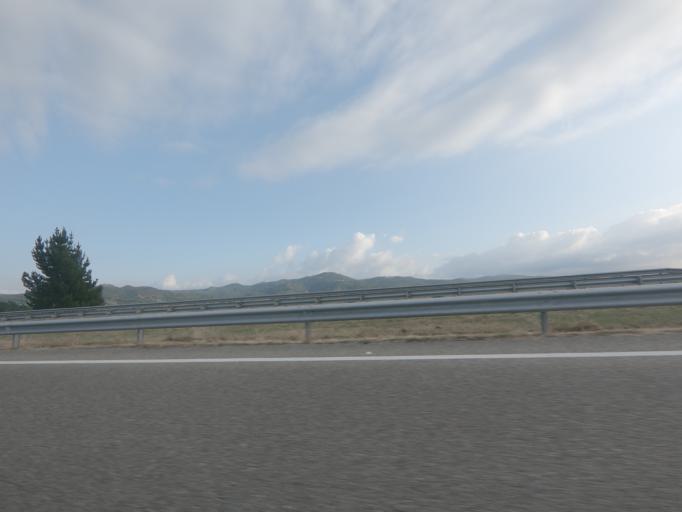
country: ES
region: Galicia
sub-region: Provincia de Ourense
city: Allariz
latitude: 42.2039
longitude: -7.8001
